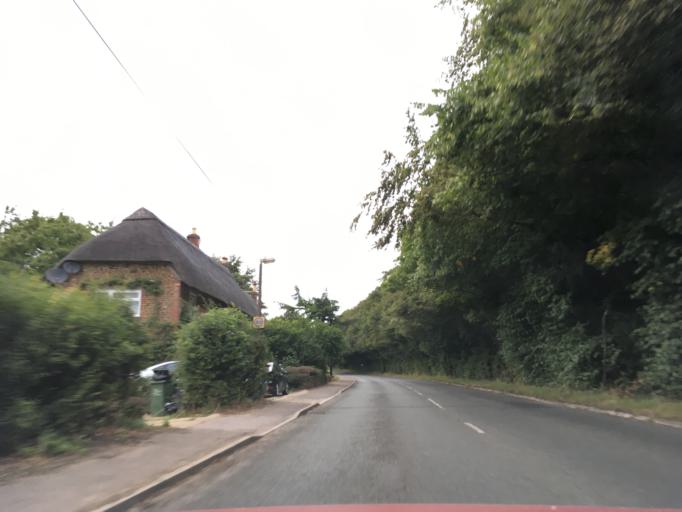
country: GB
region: England
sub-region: Wiltshire
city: Bremhill
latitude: 51.4304
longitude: -2.0630
